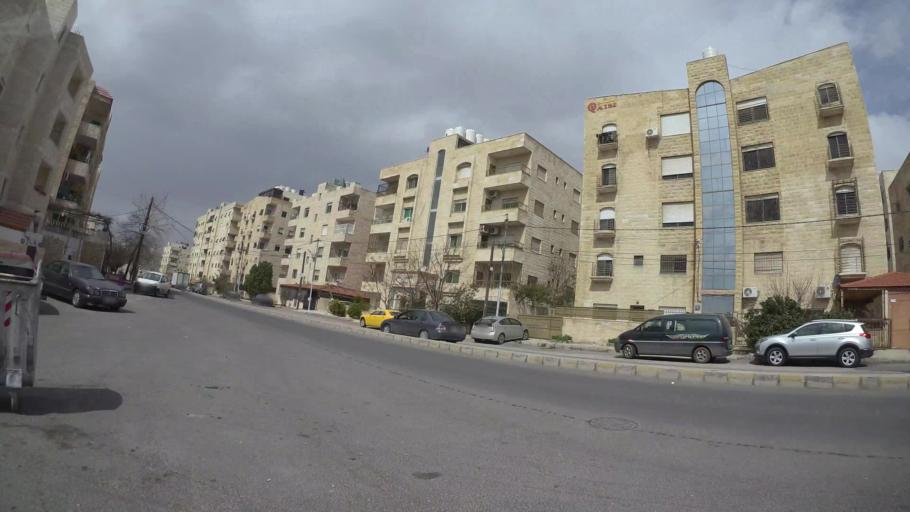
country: JO
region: Amman
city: Amman
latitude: 31.9878
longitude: 35.9218
